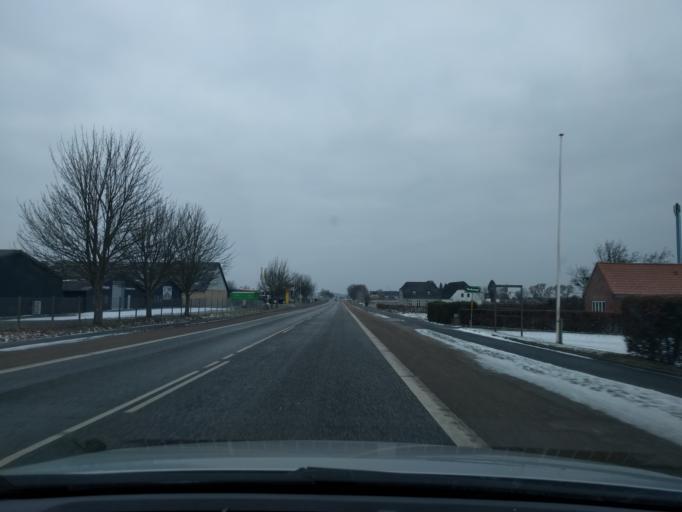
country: DK
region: South Denmark
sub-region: Middelfart Kommune
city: Strib
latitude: 55.4940
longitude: 9.7818
